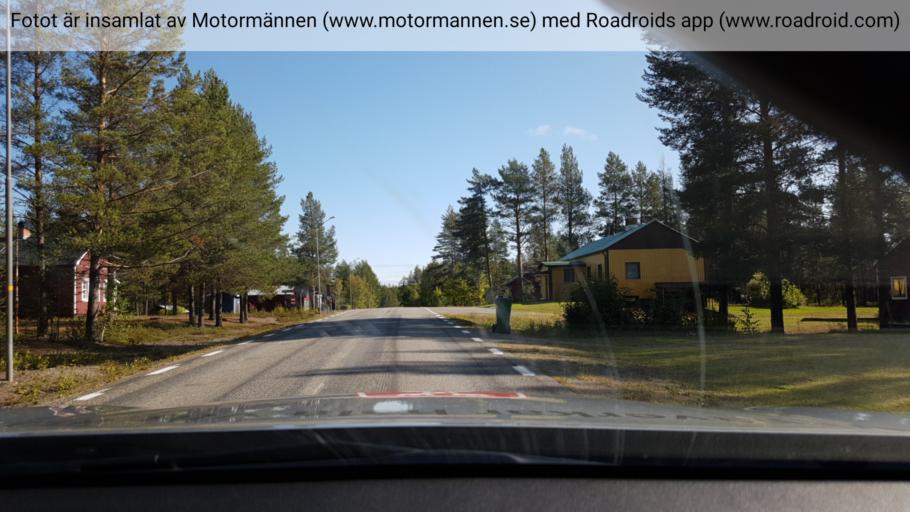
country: SE
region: Vaesterbotten
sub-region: Norsjo Kommun
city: Norsjoe
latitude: 65.1378
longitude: 19.3075
